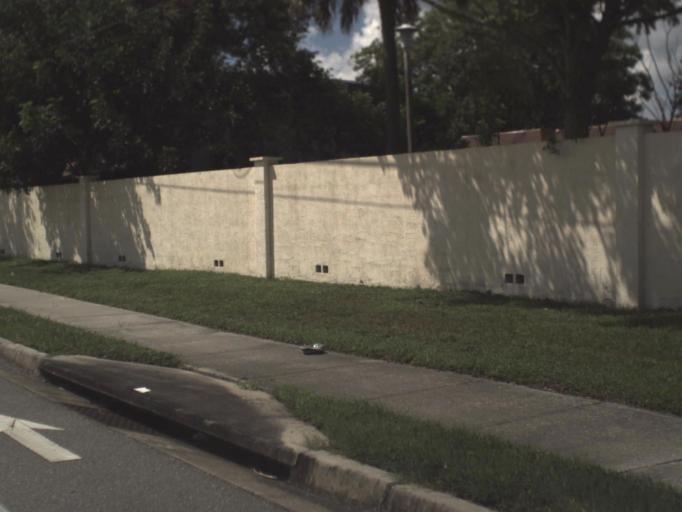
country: US
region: Florida
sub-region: Sarasota County
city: Kensington Park
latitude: 27.3376
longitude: -82.4934
